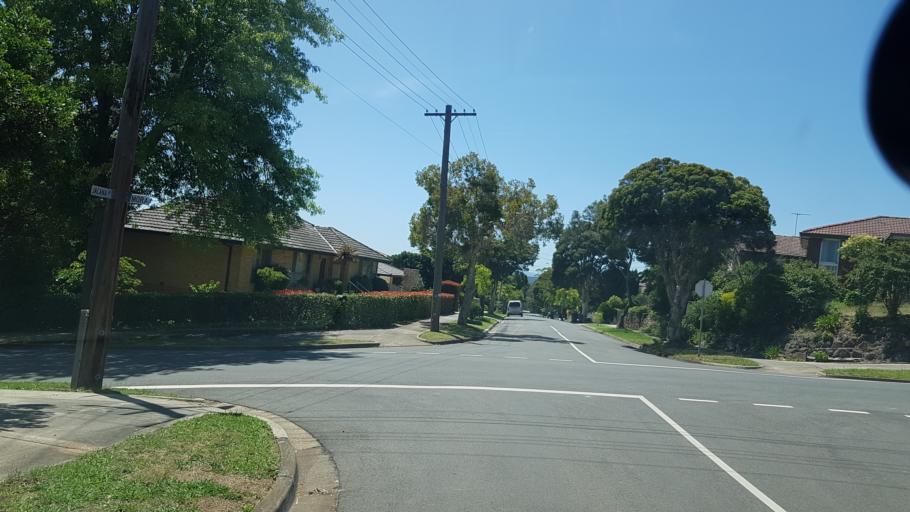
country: AU
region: Victoria
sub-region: Manningham
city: Templestowe Lower
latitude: -37.7600
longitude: 145.1023
